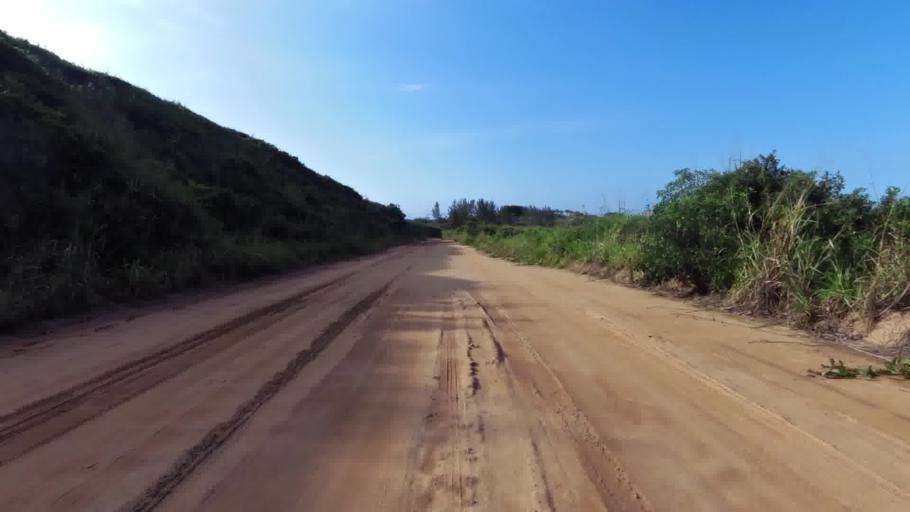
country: BR
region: Espirito Santo
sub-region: Piuma
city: Piuma
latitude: -20.8110
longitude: -40.6118
